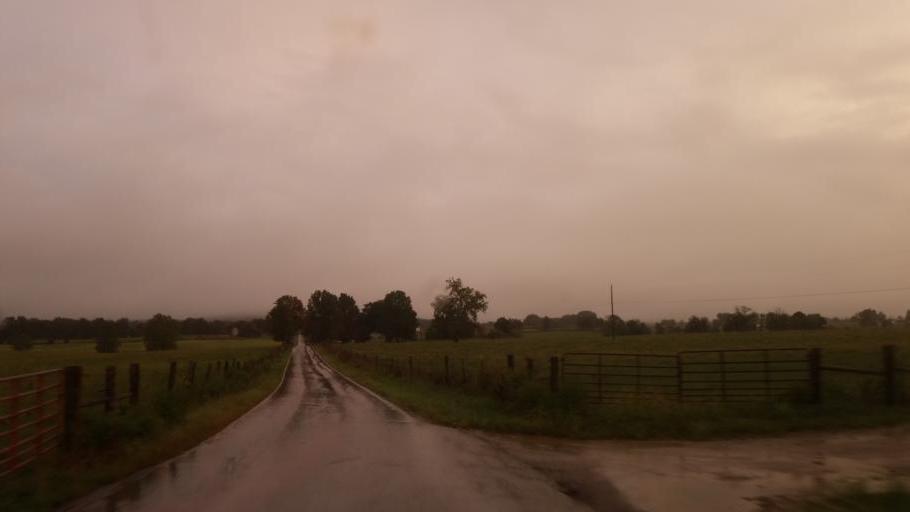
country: US
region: Kentucky
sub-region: Fleming County
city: Flemingsburg
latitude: 38.4538
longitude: -83.6435
